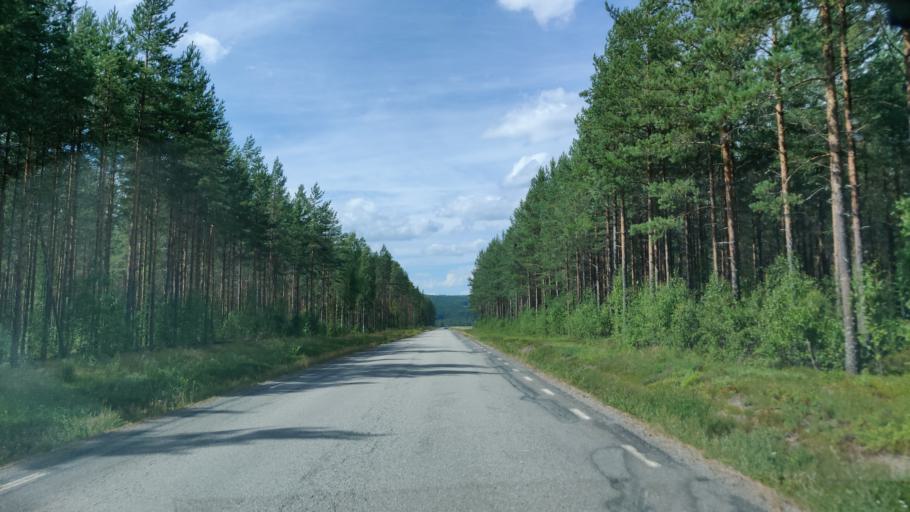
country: SE
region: Vaermland
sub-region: Hagfors Kommun
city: Ekshaerad
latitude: 60.0720
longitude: 13.5115
